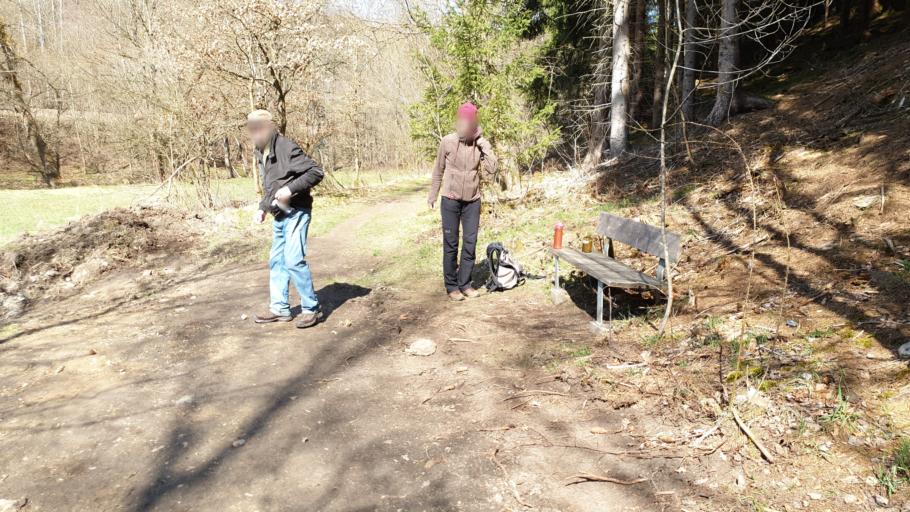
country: DE
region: Saxony
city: Gelenau
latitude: 50.7417
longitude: 12.9721
